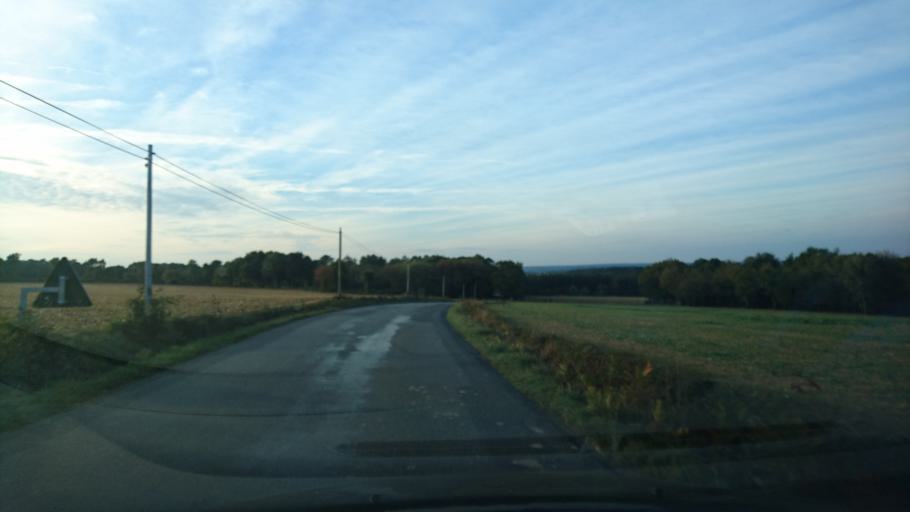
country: FR
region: Brittany
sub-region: Departement d'Ille-et-Vilaine
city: Sixt-sur-Aff
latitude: 47.7635
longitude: -2.0687
